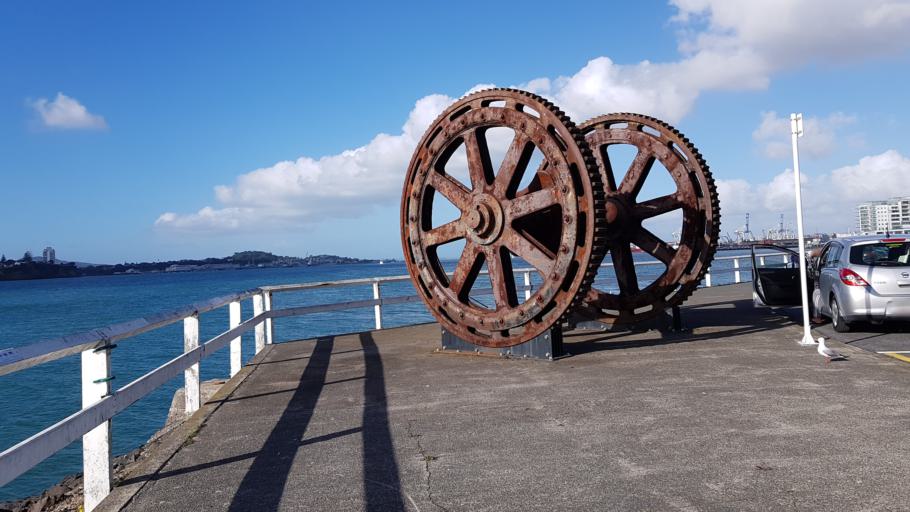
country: NZ
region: Auckland
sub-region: Auckland
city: Auckland
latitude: -36.8365
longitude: 174.7591
